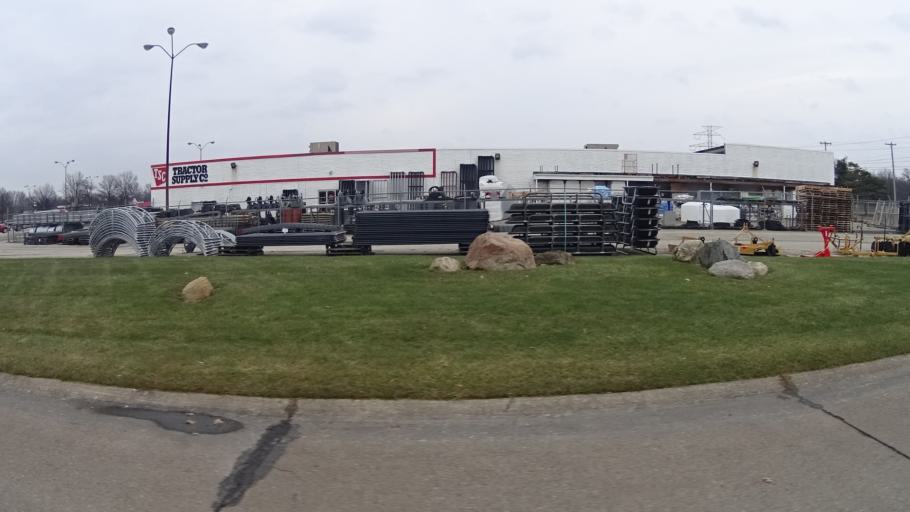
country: US
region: Ohio
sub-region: Lorain County
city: Amherst
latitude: 41.4163
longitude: -82.2038
